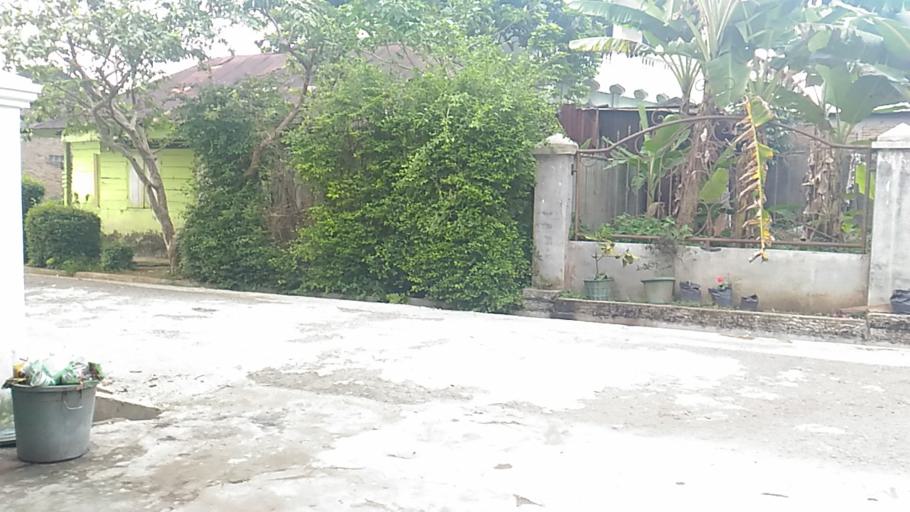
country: ID
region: North Sumatra
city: Deli Tua
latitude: 3.4703
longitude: 98.5967
